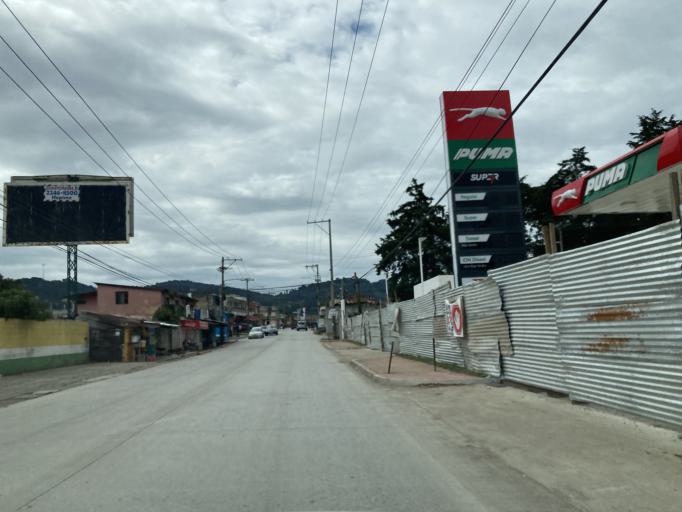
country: GT
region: Guatemala
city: San Jose Pinula
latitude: 14.5409
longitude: -90.4066
